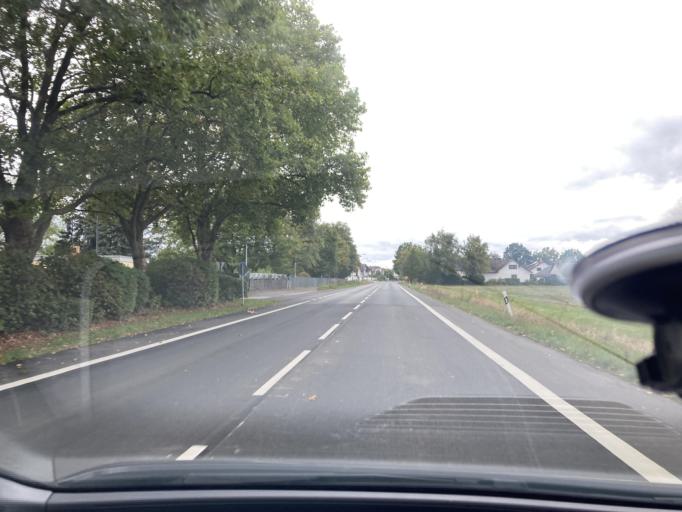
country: DE
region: Bavaria
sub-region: Regierungsbezirk Unterfranken
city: Kahl am Main
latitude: 50.0379
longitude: 9.0189
